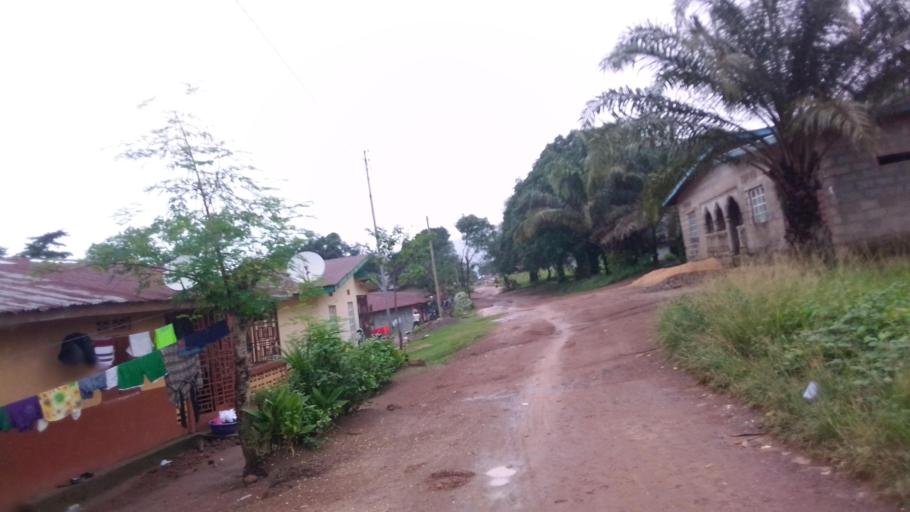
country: SL
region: Eastern Province
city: Kenema
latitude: 7.8860
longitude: -11.1703
